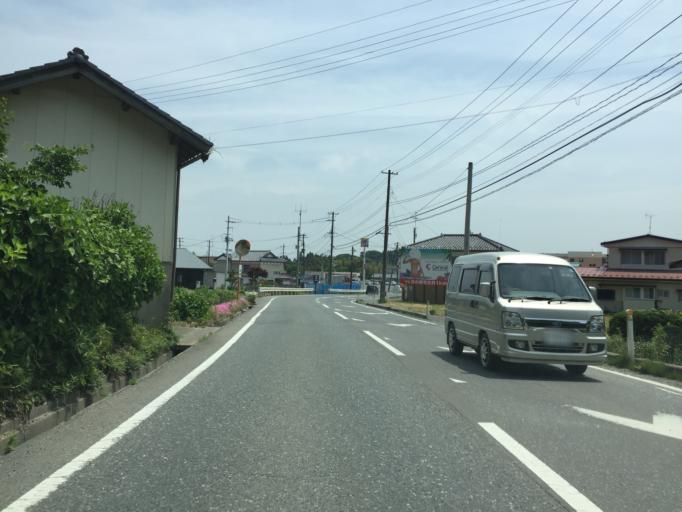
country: JP
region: Fukushima
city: Namie
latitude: 37.6441
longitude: 140.9339
